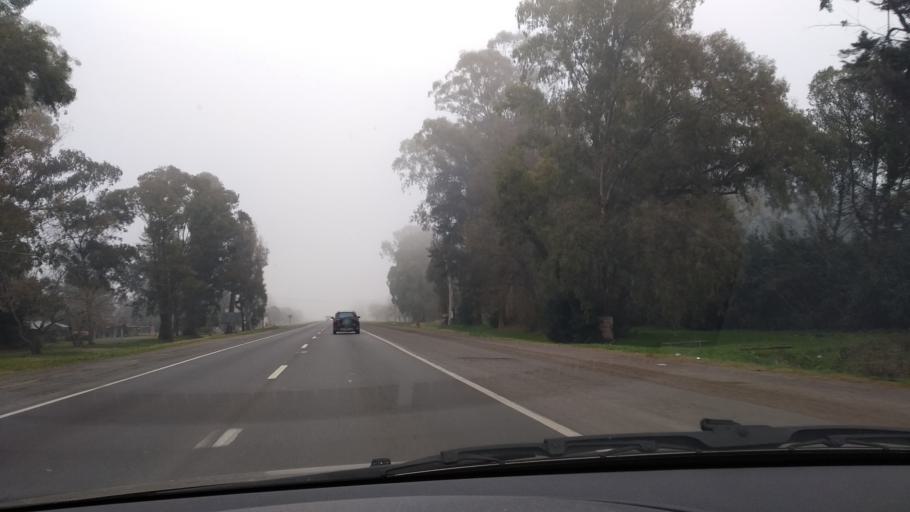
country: AR
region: Buenos Aires
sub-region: Partido de Azul
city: Azul
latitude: -36.8224
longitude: -59.8764
